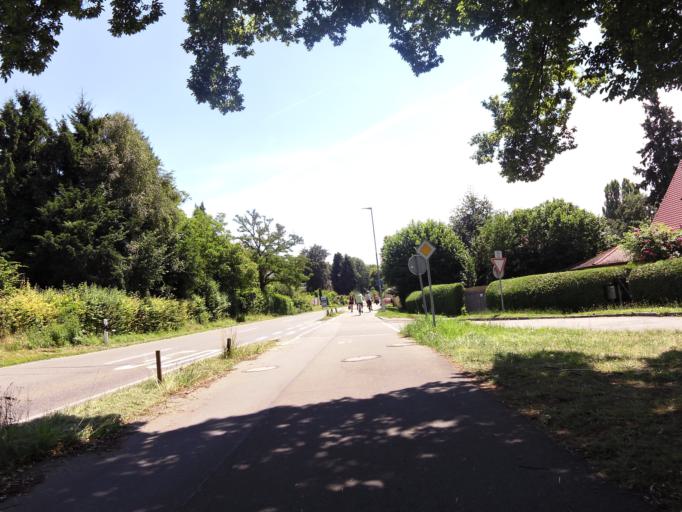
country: DE
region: Baden-Wuerttemberg
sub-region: Tuebingen Region
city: Uhldingen-Muhlhofen
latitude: 47.7146
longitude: 9.2374
